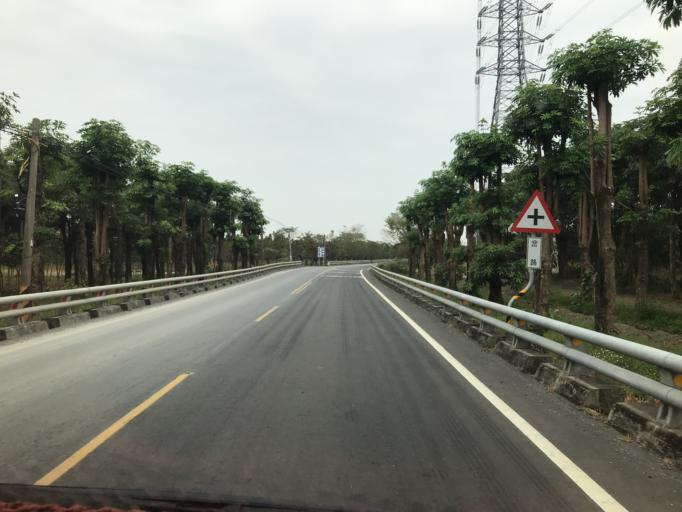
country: TW
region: Taiwan
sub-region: Pingtung
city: Pingtung
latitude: 22.4368
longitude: 120.6045
